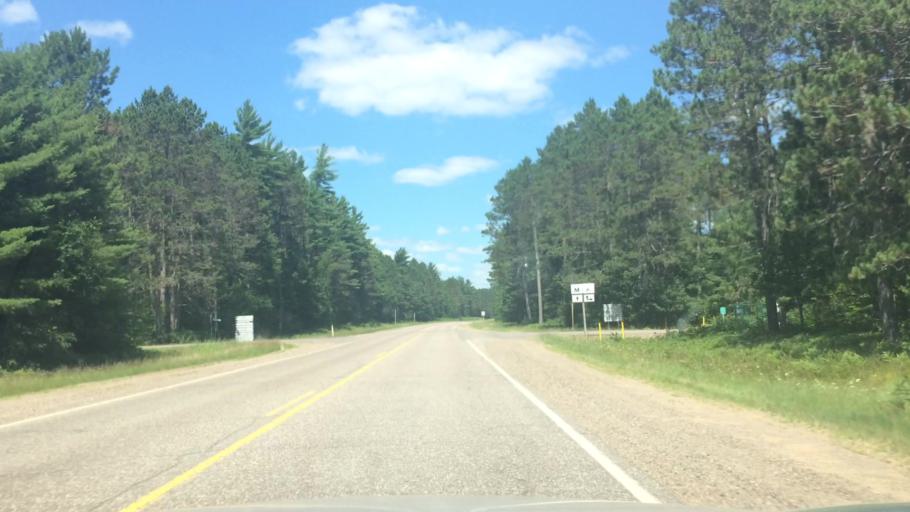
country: US
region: Wisconsin
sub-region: Vilas County
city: Lac du Flambeau
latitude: 46.0830
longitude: -89.6450
